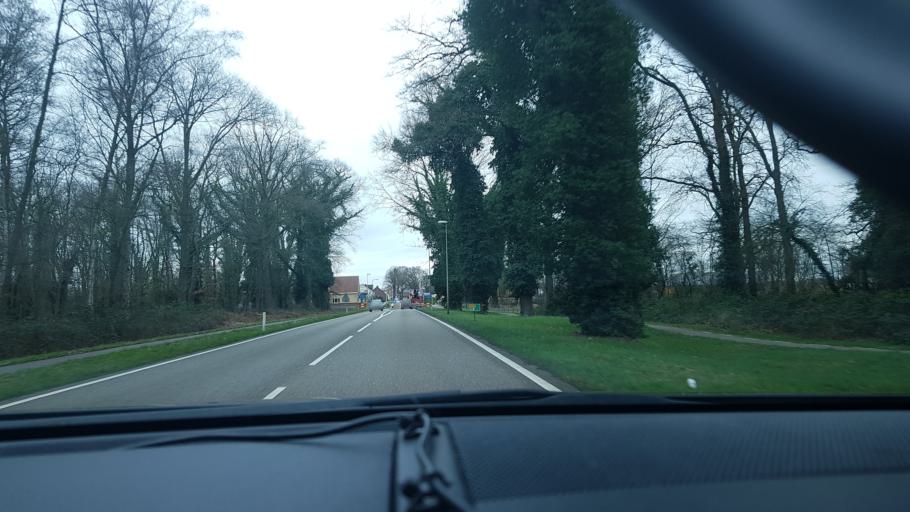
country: NL
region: Limburg
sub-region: Gemeente Leudal
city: Heythuysen
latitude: 51.2404
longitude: 5.9048
